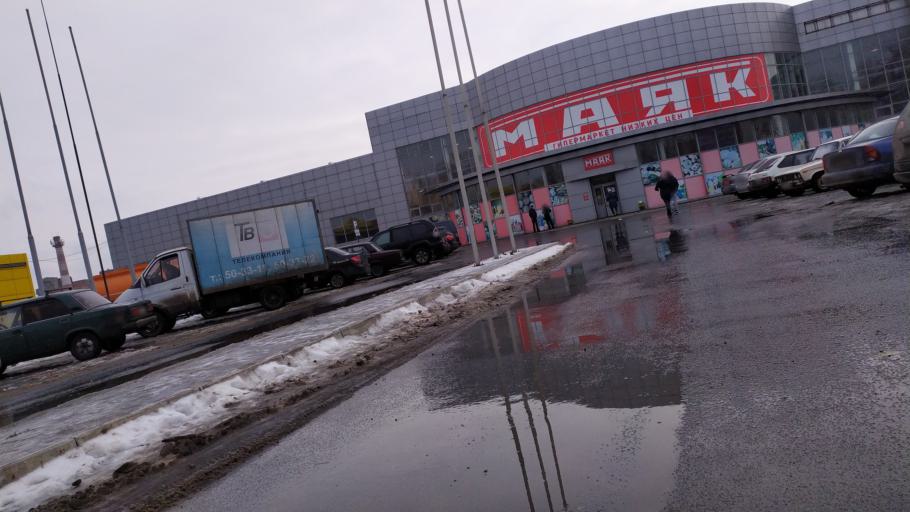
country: RU
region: Kursk
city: Kursk
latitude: 51.6594
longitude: 36.1357
